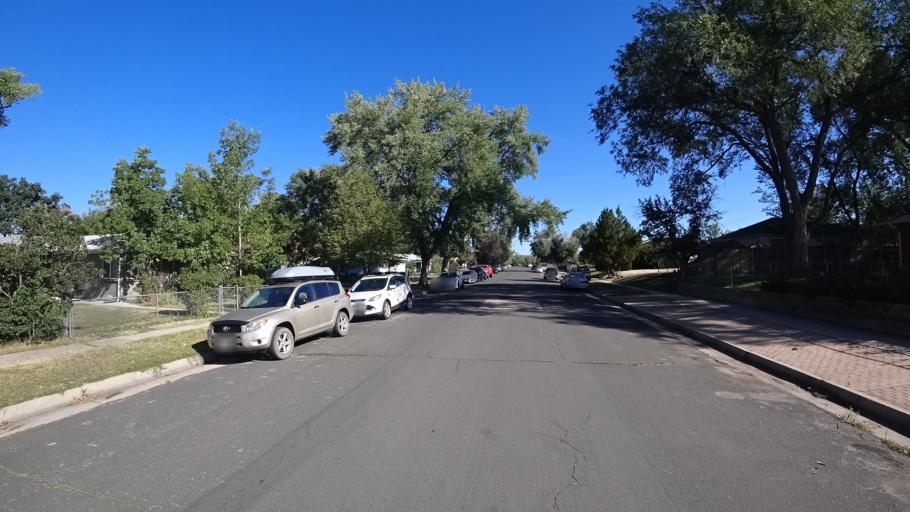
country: US
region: Colorado
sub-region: El Paso County
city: Colorado Springs
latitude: 38.8532
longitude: -104.8049
